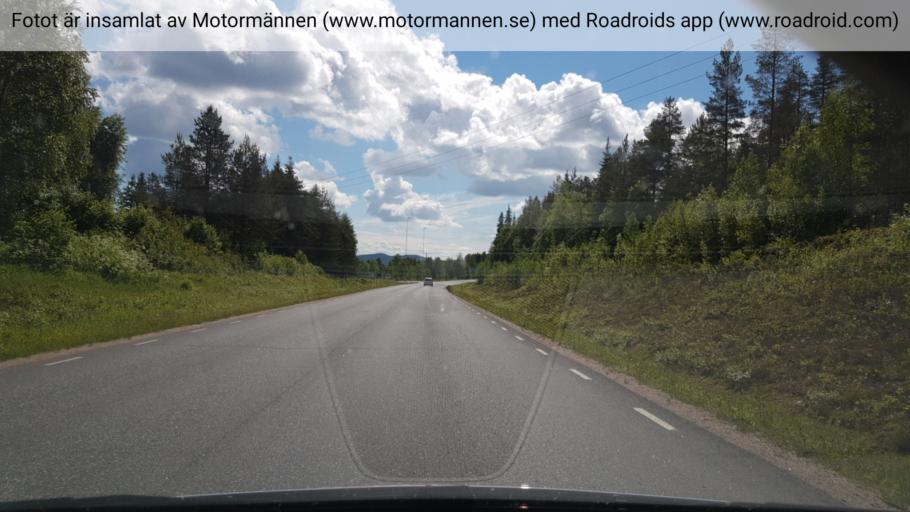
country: SE
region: Norrbotten
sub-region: Overtornea Kommun
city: OEvertornea
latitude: 66.3833
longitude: 23.6409
